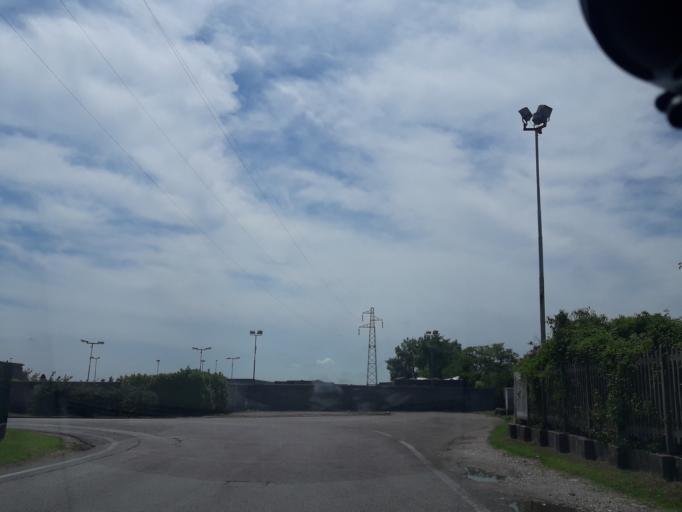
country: IT
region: Friuli Venezia Giulia
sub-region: Provincia di Udine
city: Udine
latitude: 46.0410
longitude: 13.2433
